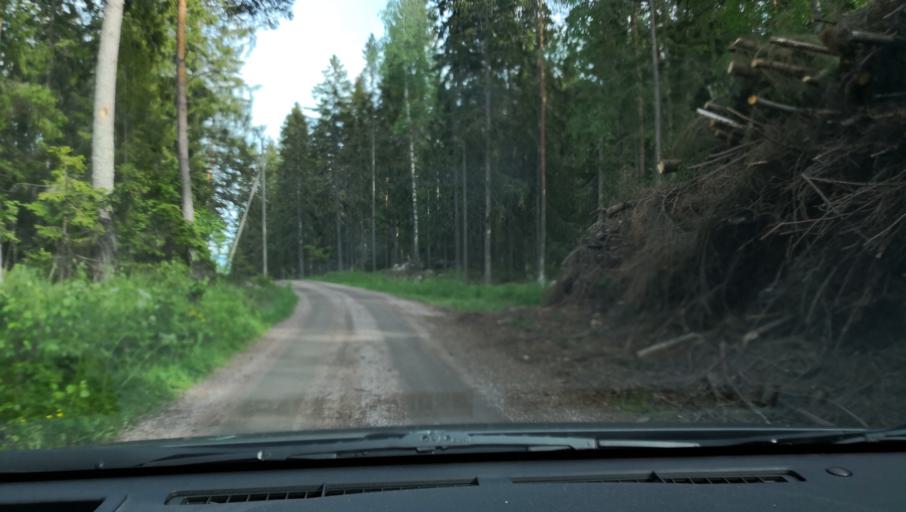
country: SE
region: Vaestmanland
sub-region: Kungsors Kommun
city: Kungsoer
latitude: 59.3601
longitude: 16.0277
